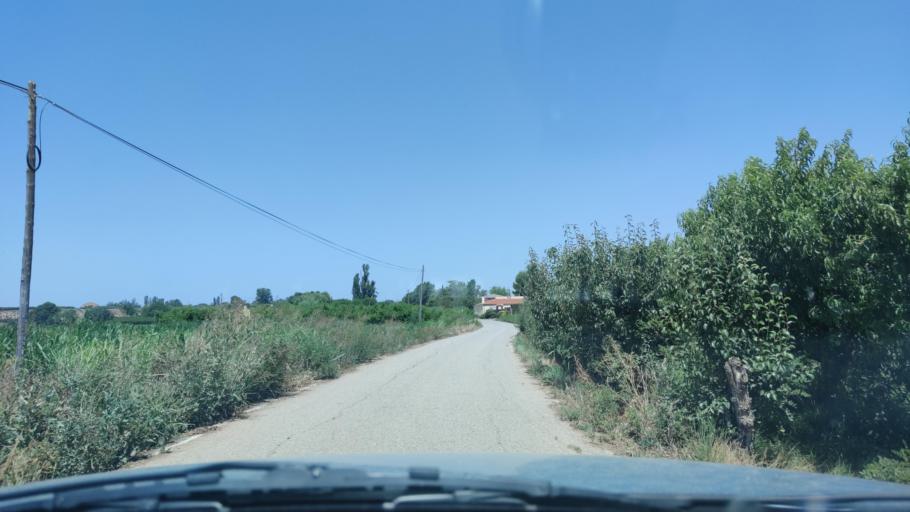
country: ES
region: Catalonia
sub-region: Provincia de Lleida
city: Torrefarrera
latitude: 41.6497
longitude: 0.5943
